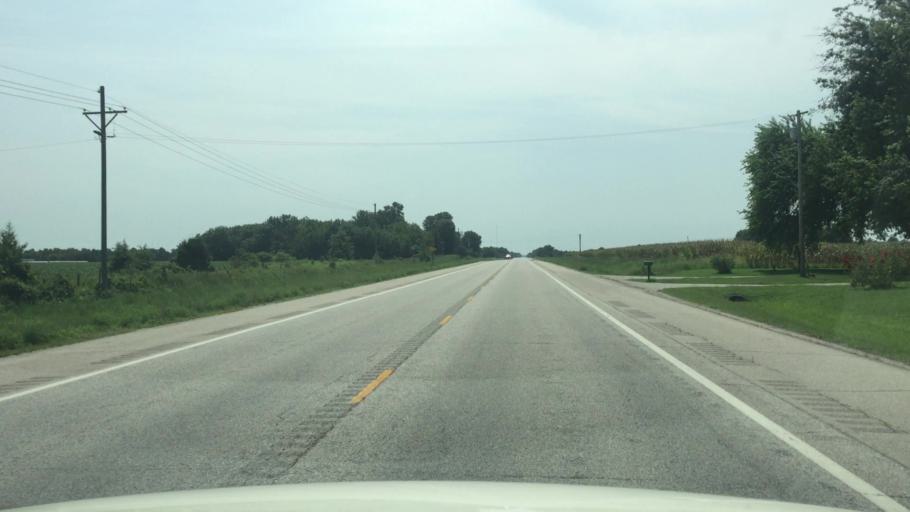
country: US
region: Kansas
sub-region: Cherokee County
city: Galena
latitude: 37.1527
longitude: -94.7043
